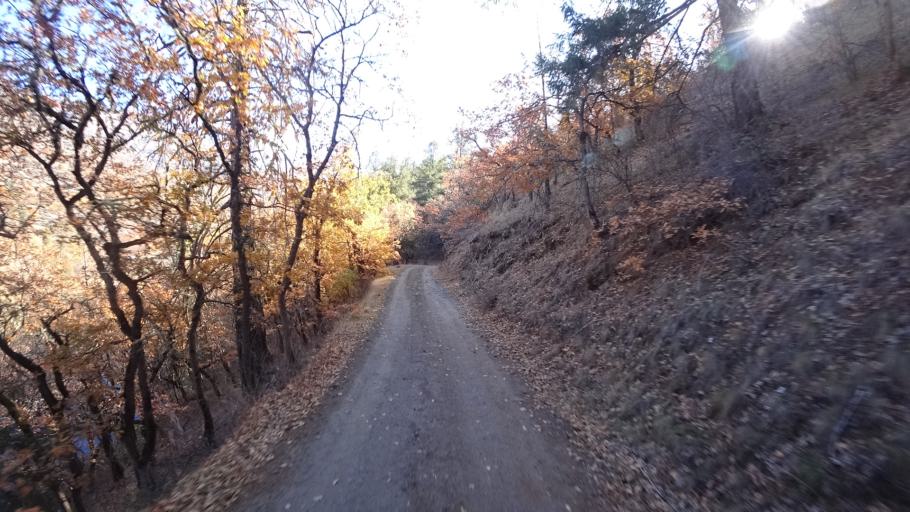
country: US
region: California
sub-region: Siskiyou County
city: Yreka
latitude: 41.8667
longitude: -122.8106
